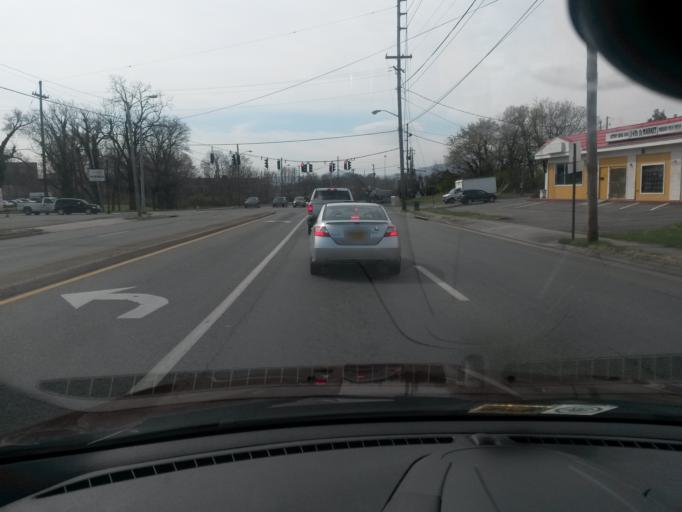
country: US
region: Virginia
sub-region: City of Roanoke
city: Roanoke
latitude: 37.2831
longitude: -79.9768
